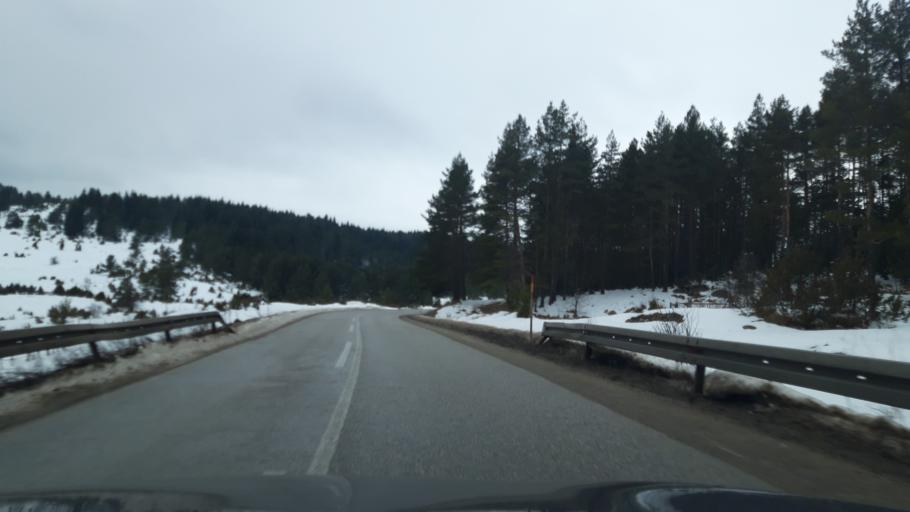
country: BA
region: Republika Srpska
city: Sokolac
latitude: 43.9099
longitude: 18.7048
